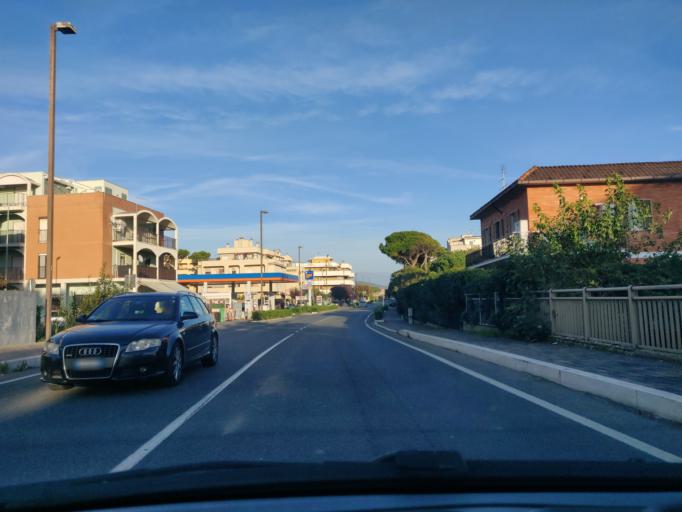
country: IT
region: Latium
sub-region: Citta metropolitana di Roma Capitale
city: Santa Marinella
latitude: 42.0384
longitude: 11.8776
